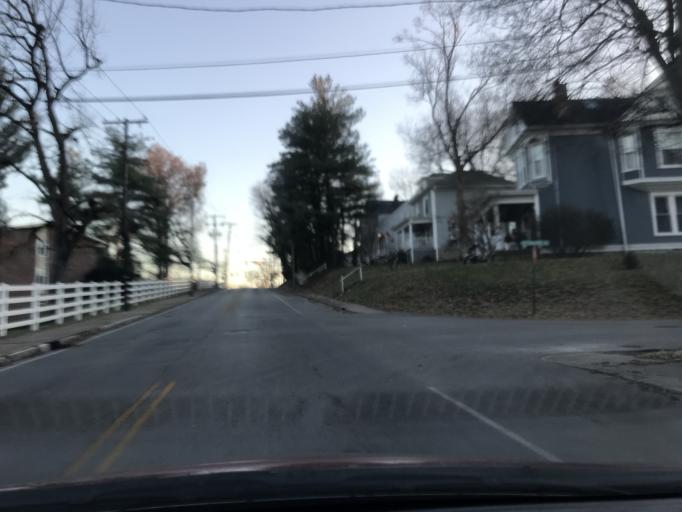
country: US
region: Kentucky
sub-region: Jefferson County
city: Indian Hills
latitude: 38.2552
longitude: -85.7005
